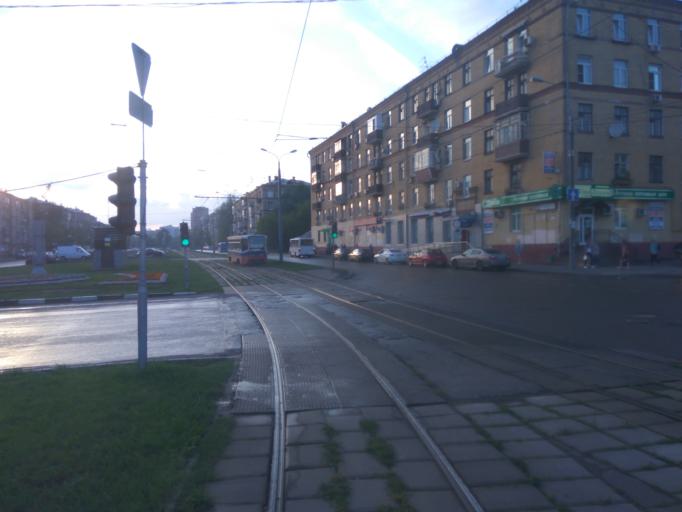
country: RU
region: Moskovskaya
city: Bogorodskoye
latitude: 55.8152
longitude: 37.7325
